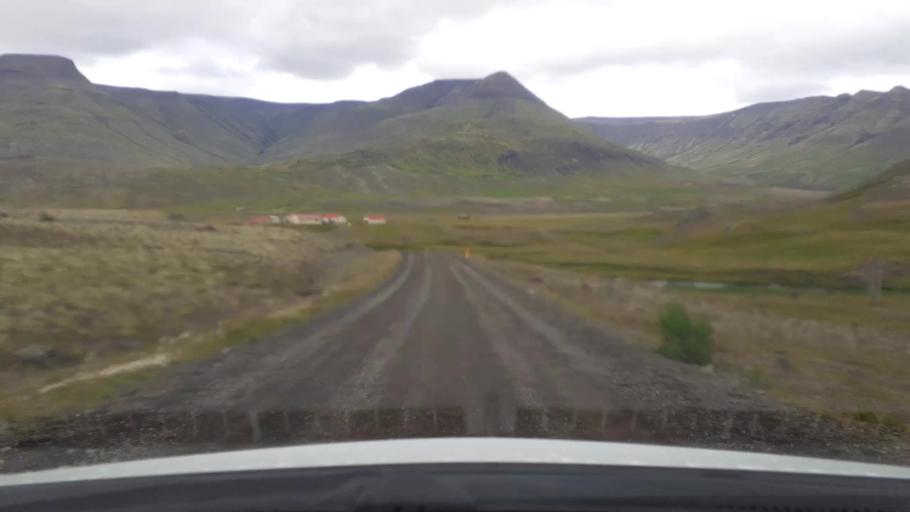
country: IS
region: Capital Region
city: Mosfellsbaer
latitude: 64.2050
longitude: -21.5622
